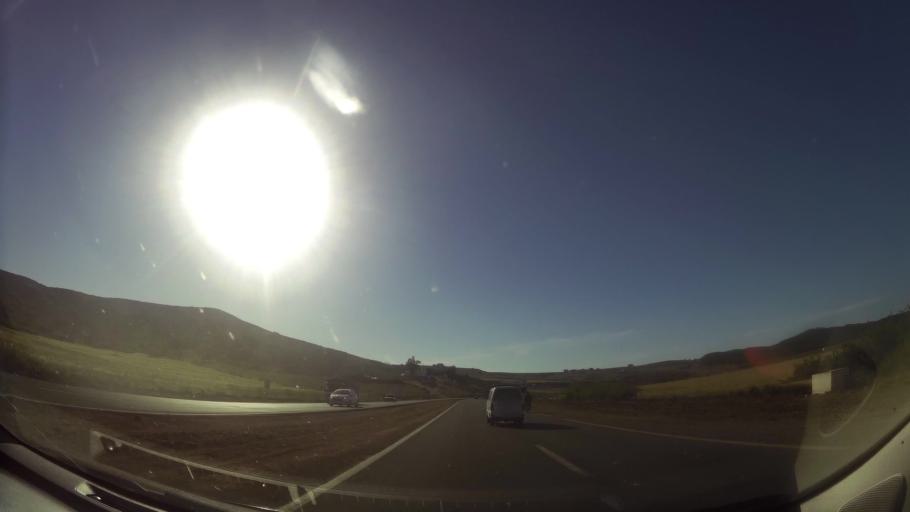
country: MA
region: Oriental
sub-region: Berkane-Taourirt
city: Madagh
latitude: 35.0444
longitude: -2.2158
